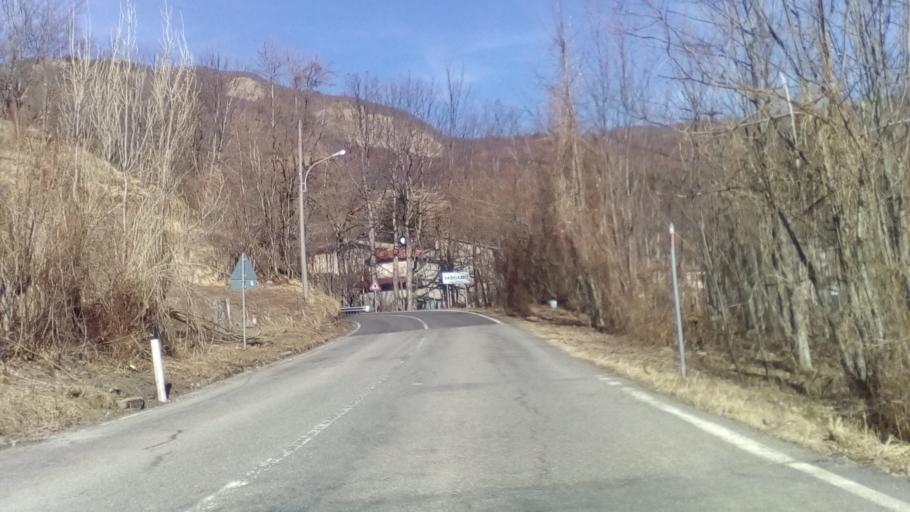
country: IT
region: Emilia-Romagna
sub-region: Provincia di Modena
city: Riolunato
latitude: 44.2618
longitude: 10.6485
